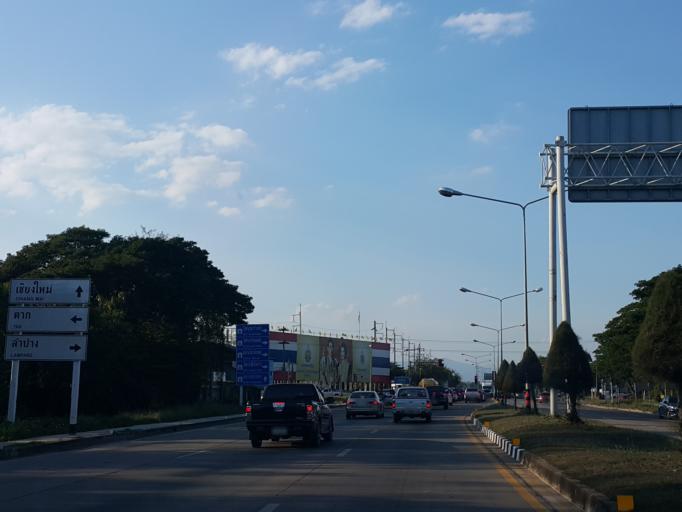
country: TH
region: Lampang
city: Lampang
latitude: 18.2654
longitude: 99.4666
